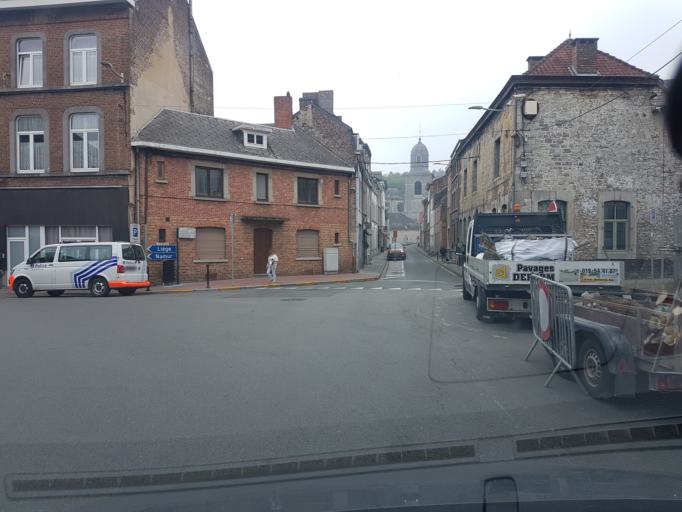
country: BE
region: Wallonia
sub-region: Province de Namur
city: Andenne
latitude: 50.4862
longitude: 5.0981
